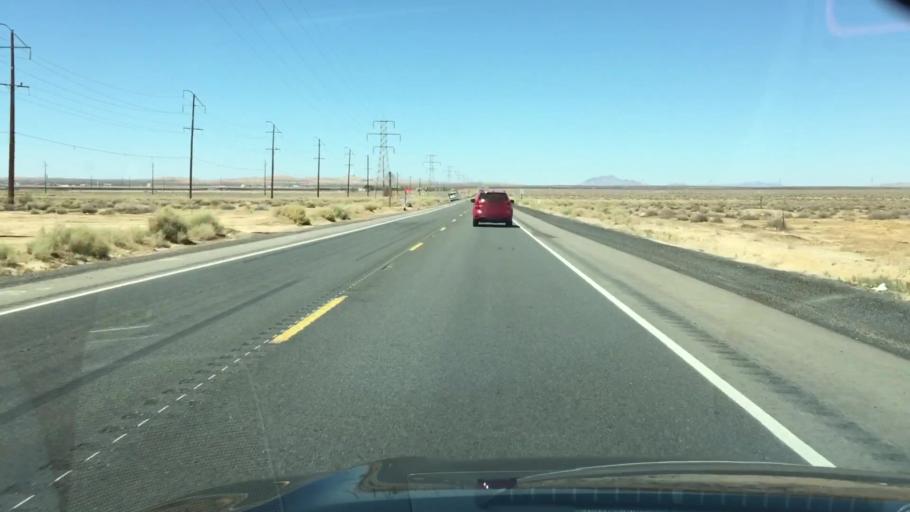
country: US
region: California
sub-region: Kern County
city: Boron
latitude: 34.9989
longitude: -117.5434
